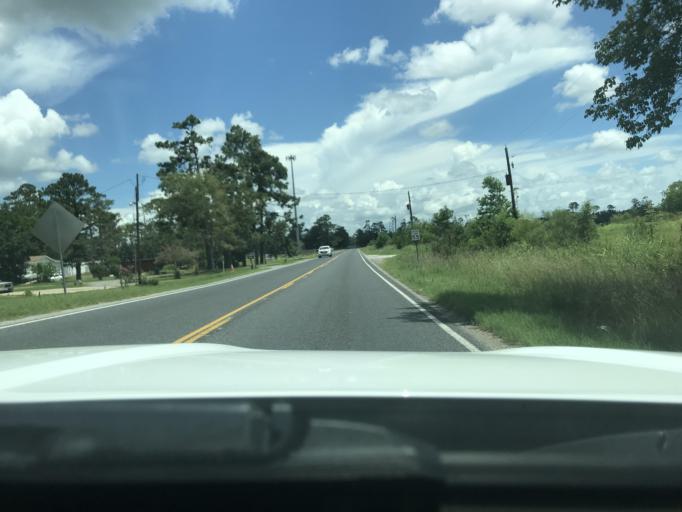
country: US
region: Louisiana
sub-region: Calcasieu Parish
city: Moss Bluff
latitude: 30.2771
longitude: -93.1809
